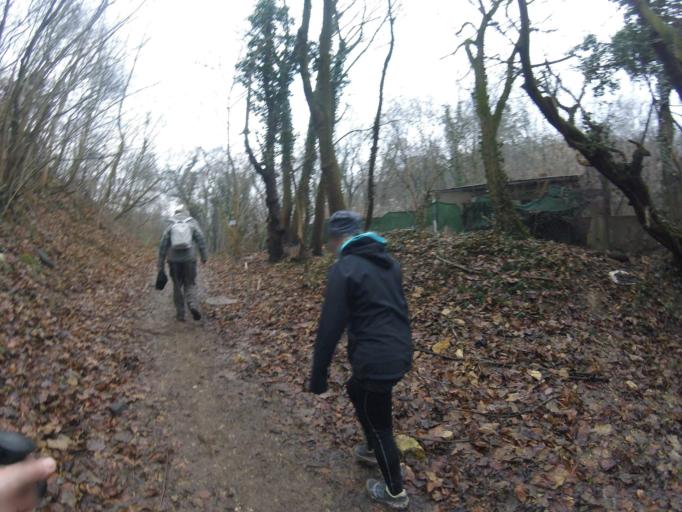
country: HU
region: Pest
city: Budakeszi
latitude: 47.5254
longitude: 18.9688
